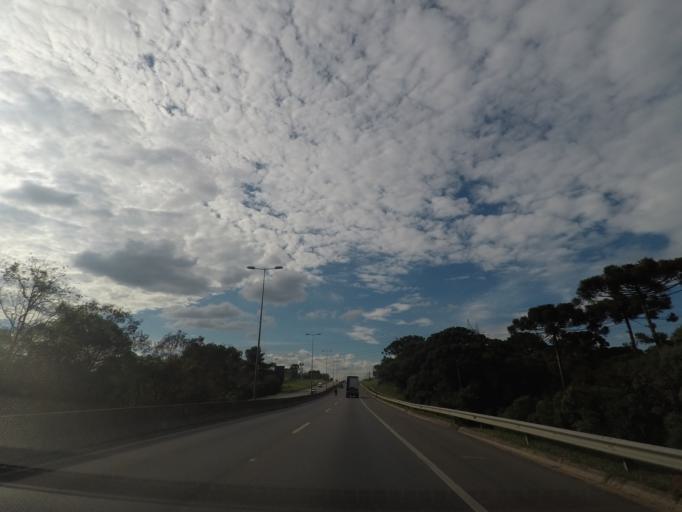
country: BR
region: Parana
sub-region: Araucaria
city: Araucaria
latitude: -25.5998
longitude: -49.3172
